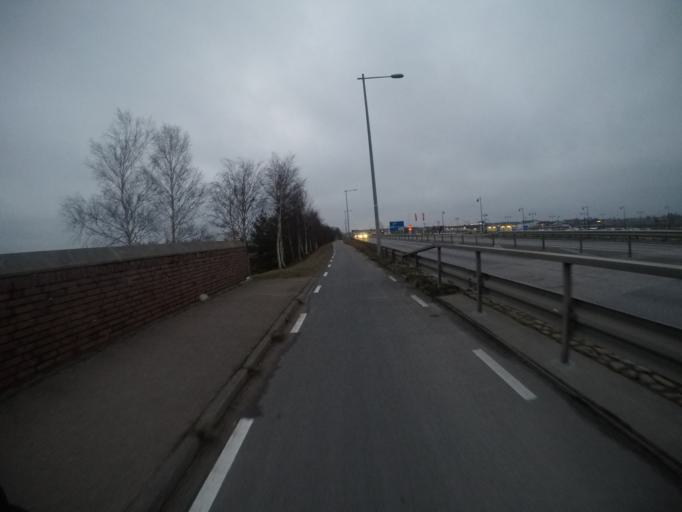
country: SE
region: Halland
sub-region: Laholms Kommun
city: Laholm
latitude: 56.5026
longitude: 12.9996
